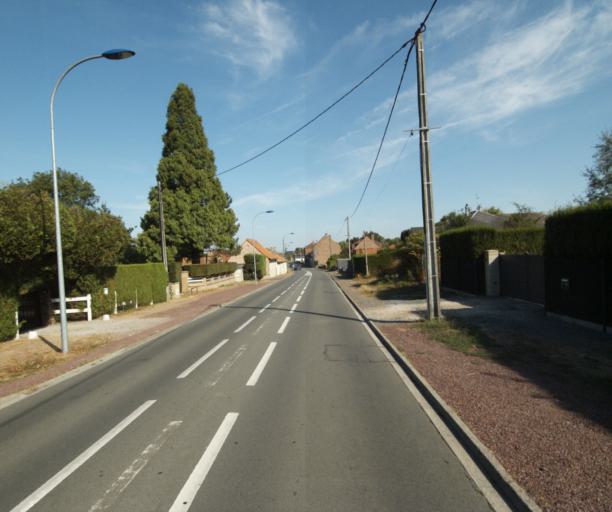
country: FR
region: Nord-Pas-de-Calais
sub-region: Departement du Nord
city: Halluin
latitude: 50.7687
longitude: 3.1423
